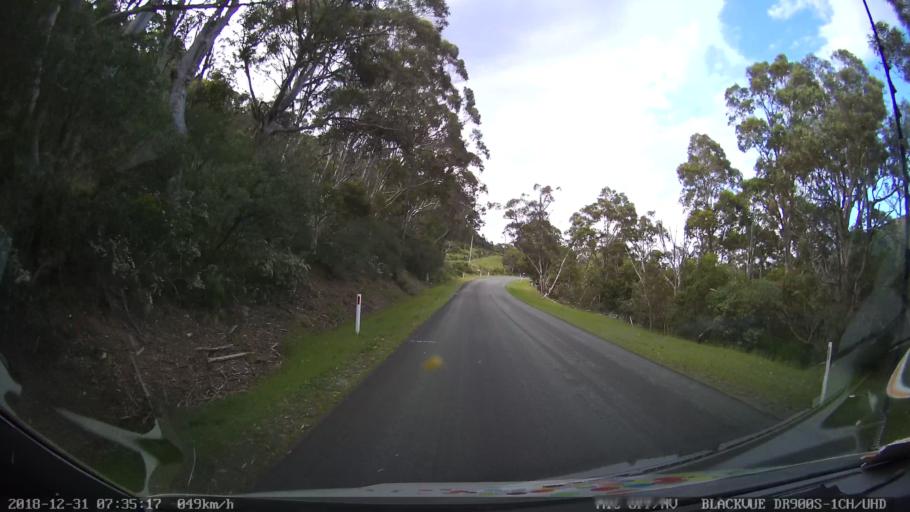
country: AU
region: New South Wales
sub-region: Snowy River
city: Jindabyne
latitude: -36.3340
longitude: 148.4454
